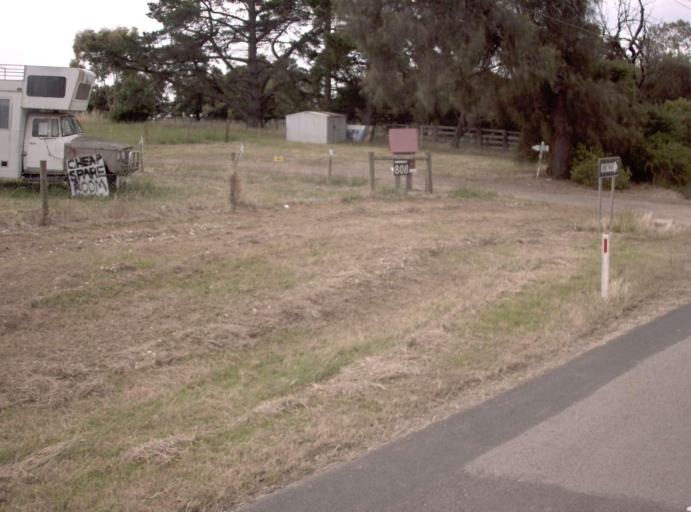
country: AU
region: Victoria
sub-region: Mornington Peninsula
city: Moorooduc
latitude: -38.2381
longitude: 145.0865
